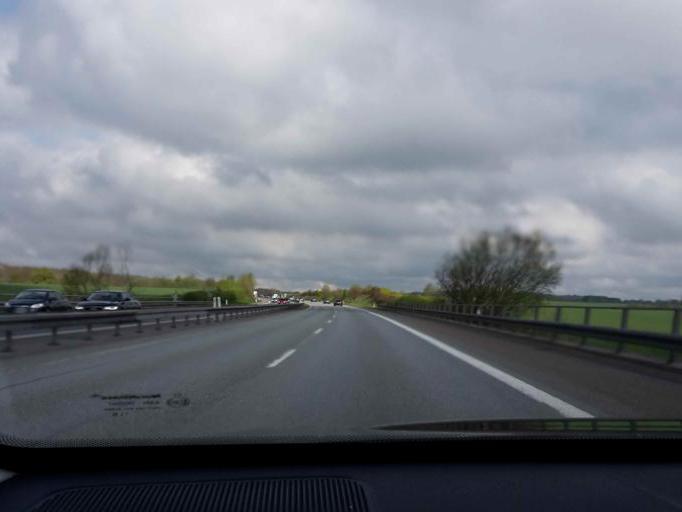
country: DK
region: South Denmark
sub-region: Fredericia Kommune
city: Taulov
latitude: 55.5881
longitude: 9.6059
